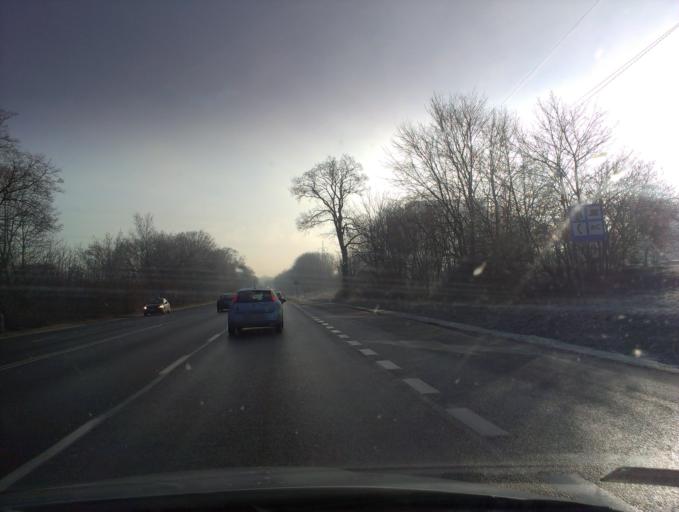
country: PL
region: Greater Poland Voivodeship
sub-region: Poznan
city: Poznan
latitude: 52.4430
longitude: 16.9222
